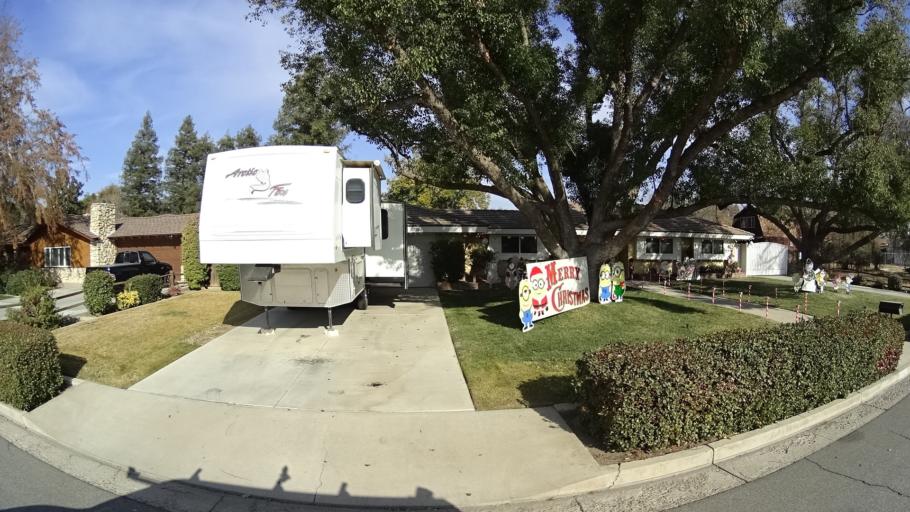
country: US
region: California
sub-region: Kern County
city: Oildale
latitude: 35.4089
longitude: -119.0669
